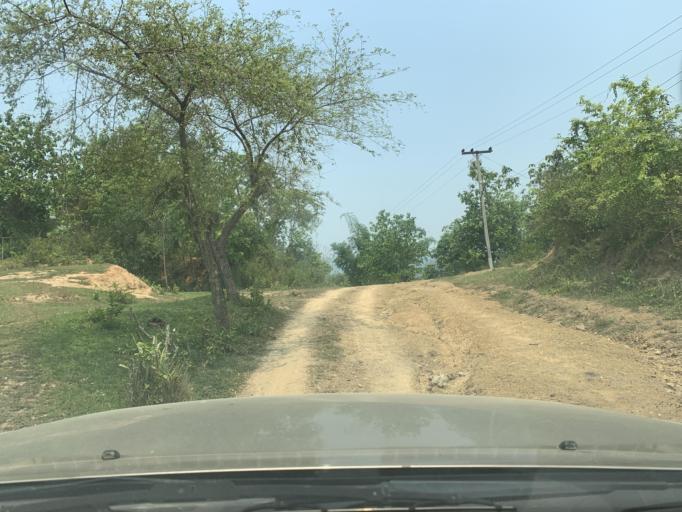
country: LA
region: Louangphabang
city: Louangphabang
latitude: 19.9470
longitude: 102.1338
